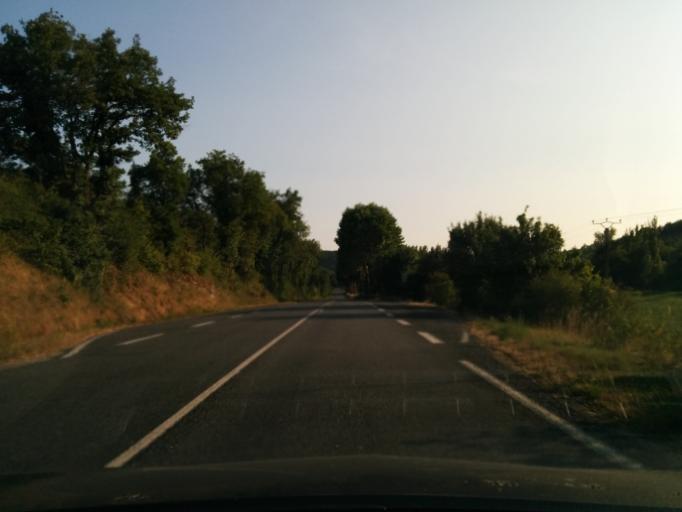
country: FR
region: Midi-Pyrenees
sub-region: Departement du Lot
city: Le Vigan
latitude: 44.6824
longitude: 1.4834
